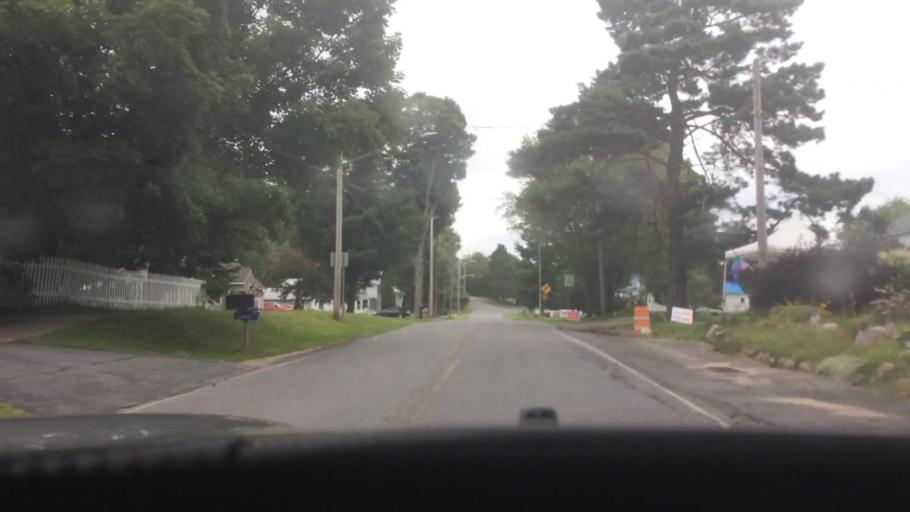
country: US
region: New York
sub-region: St. Lawrence County
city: Hannawa Falls
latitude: 44.5546
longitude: -74.9298
